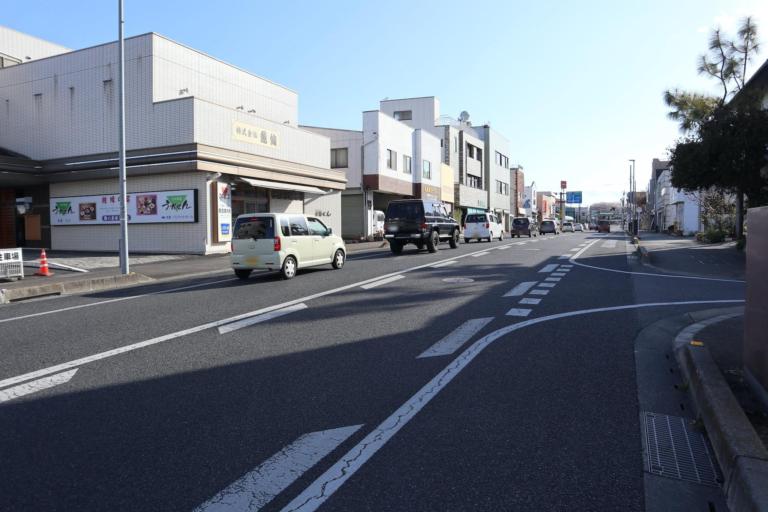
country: JP
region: Gunma
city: Kiryu
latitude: 36.3976
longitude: 139.3253
